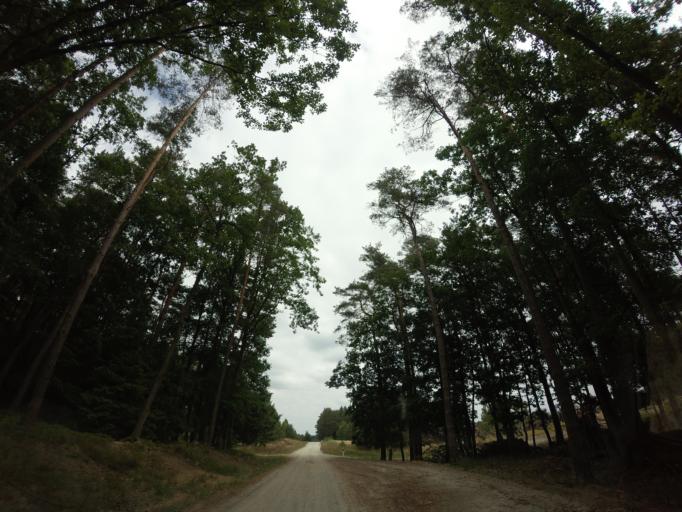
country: PL
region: Lubusz
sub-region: Powiat strzelecko-drezdenecki
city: Stare Kurowo
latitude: 52.8954
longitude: 15.6507
